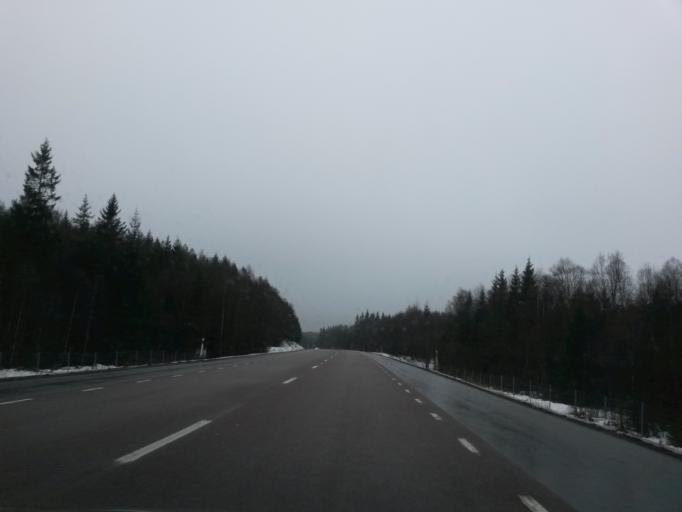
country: SE
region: Vaestra Goetaland
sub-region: Boras Kommun
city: Viskafors
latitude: 57.6227
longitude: 12.8856
